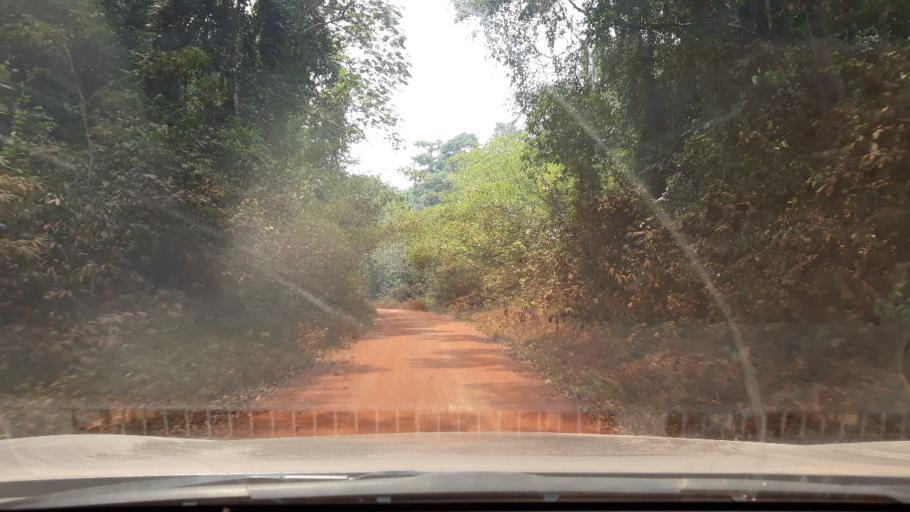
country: CD
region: Eastern Province
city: Buta
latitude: 2.3143
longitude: 25.0039
